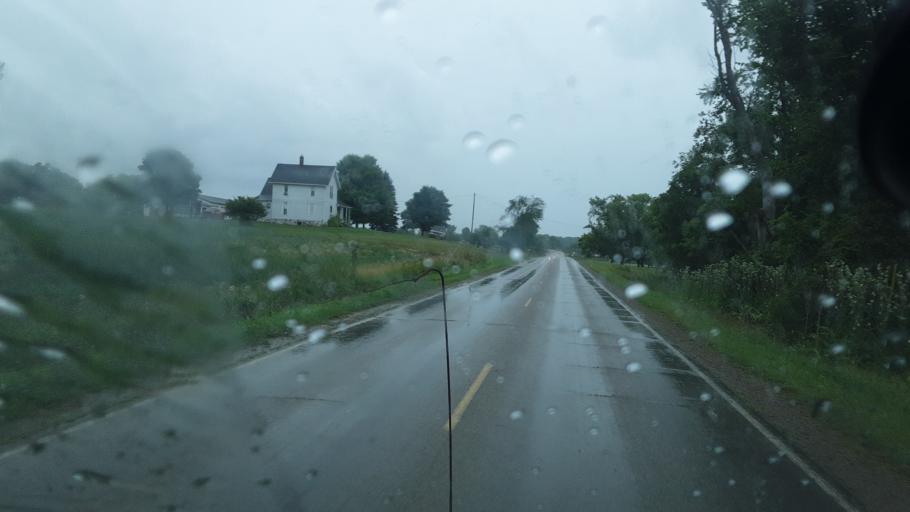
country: US
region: Ohio
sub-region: Williams County
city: Pioneer
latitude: 41.7089
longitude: -84.6428
